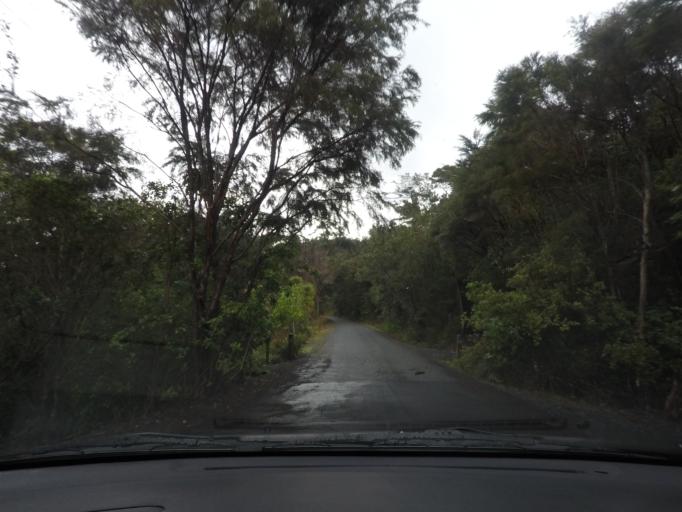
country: NZ
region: Auckland
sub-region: Auckland
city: Warkworth
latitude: -36.4762
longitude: 174.7337
